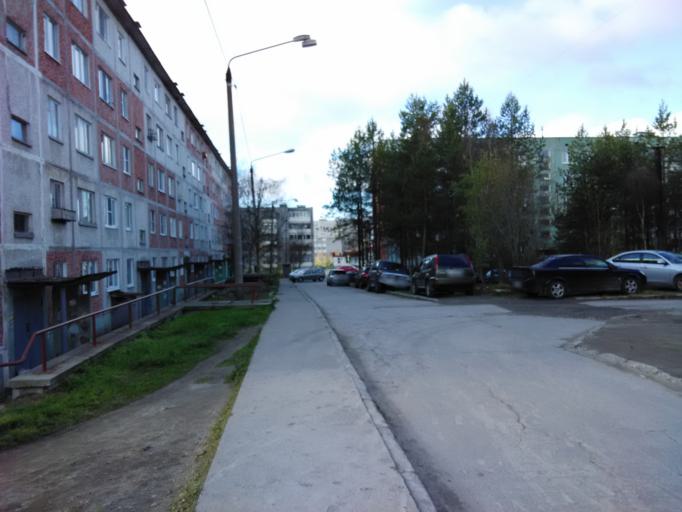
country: RU
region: Murmansk
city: Polyarnyye Zori
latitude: 67.3702
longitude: 32.4904
